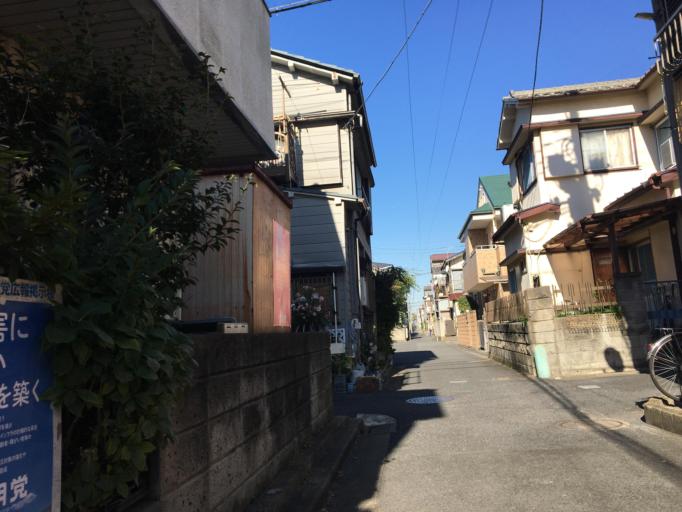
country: JP
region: Tokyo
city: Urayasu
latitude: 35.6881
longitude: 139.8930
